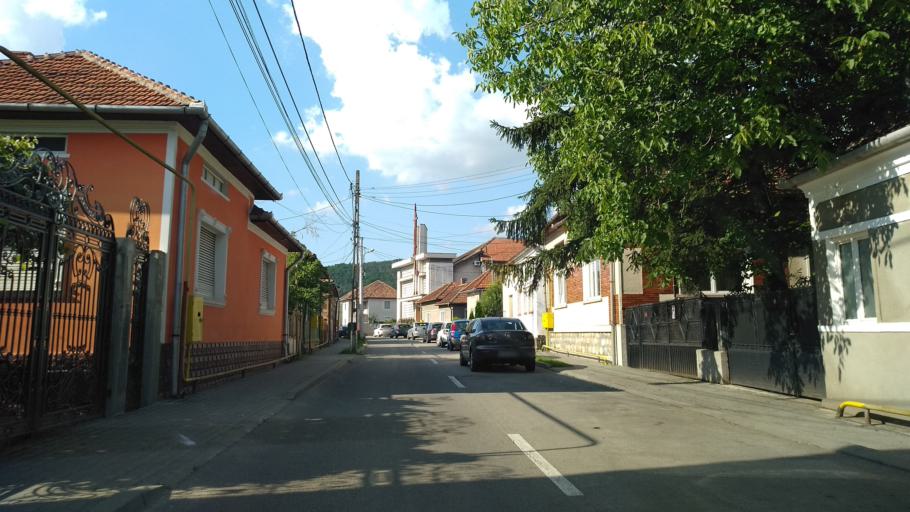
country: RO
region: Hunedoara
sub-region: Oras Hateg
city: Hateg
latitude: 45.6124
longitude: 22.9523
